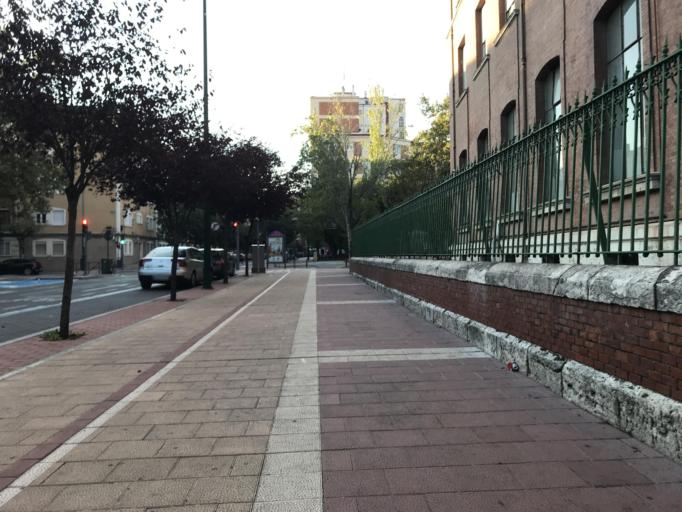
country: ES
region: Castille and Leon
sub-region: Provincia de Valladolid
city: Valladolid
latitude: 41.6551
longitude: -4.7167
